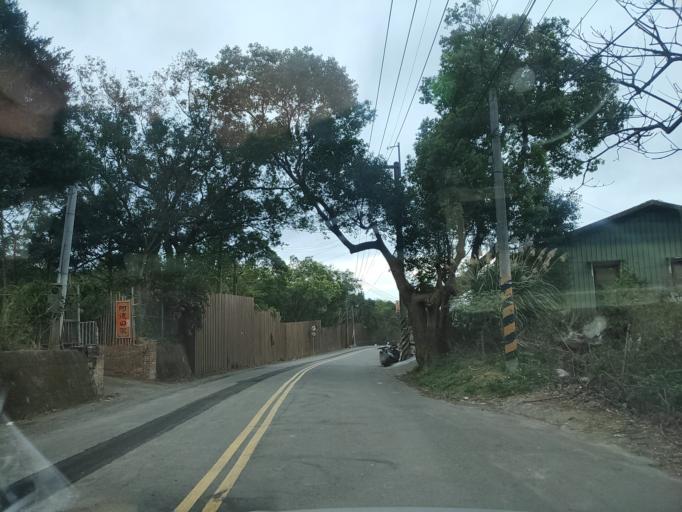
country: TW
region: Taiwan
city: Fengyuan
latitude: 24.3798
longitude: 120.7591
